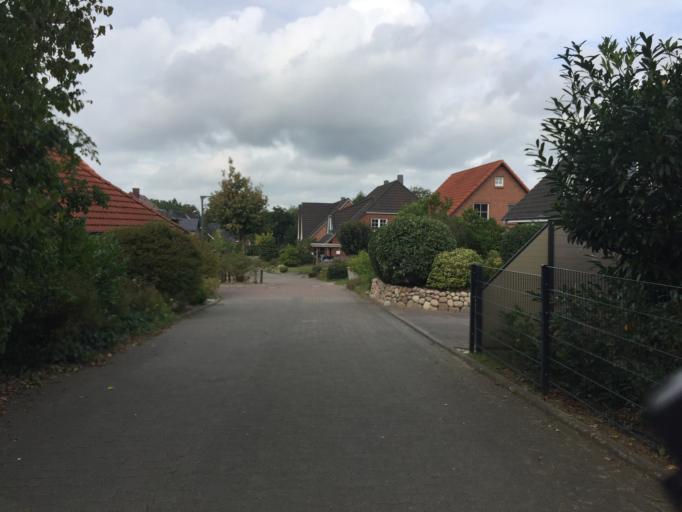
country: DE
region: Schleswig-Holstein
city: Itzehoe
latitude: 53.9329
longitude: 9.5328
